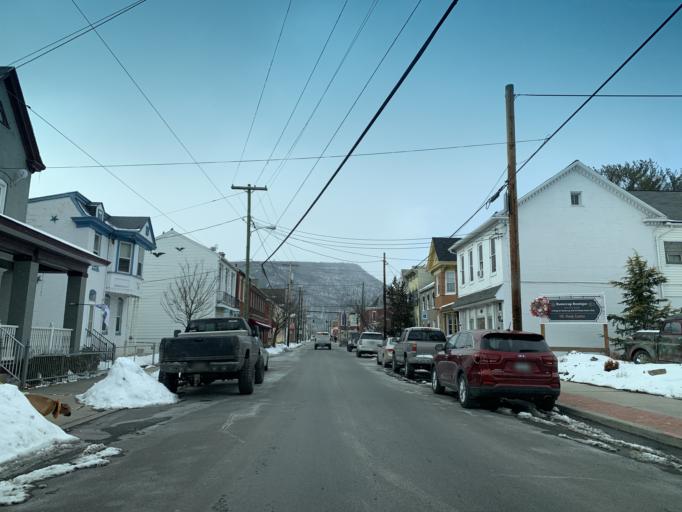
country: US
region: Maryland
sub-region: Allegany County
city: Cumberland
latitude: 39.6570
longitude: -78.7681
